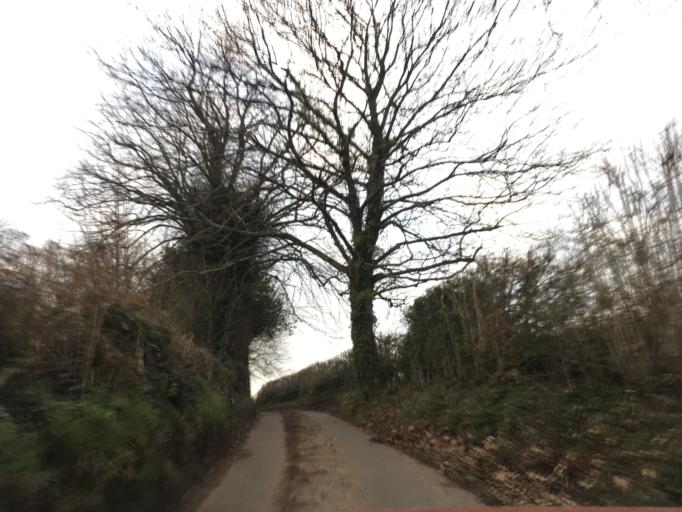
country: GB
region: Wales
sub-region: Newport
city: Marshfield
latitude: 51.5464
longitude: -3.0926
